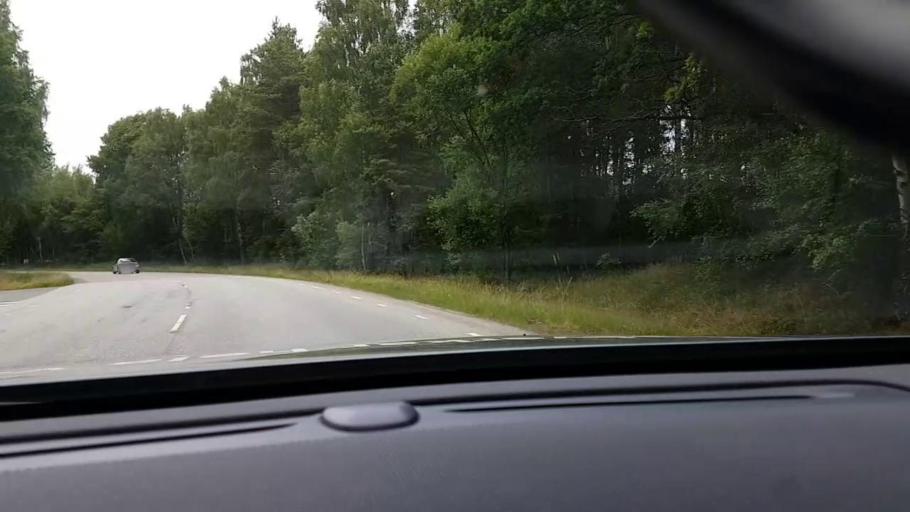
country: SE
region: Skane
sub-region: Hassleholms Kommun
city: Hassleholm
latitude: 56.1715
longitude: 13.8027
